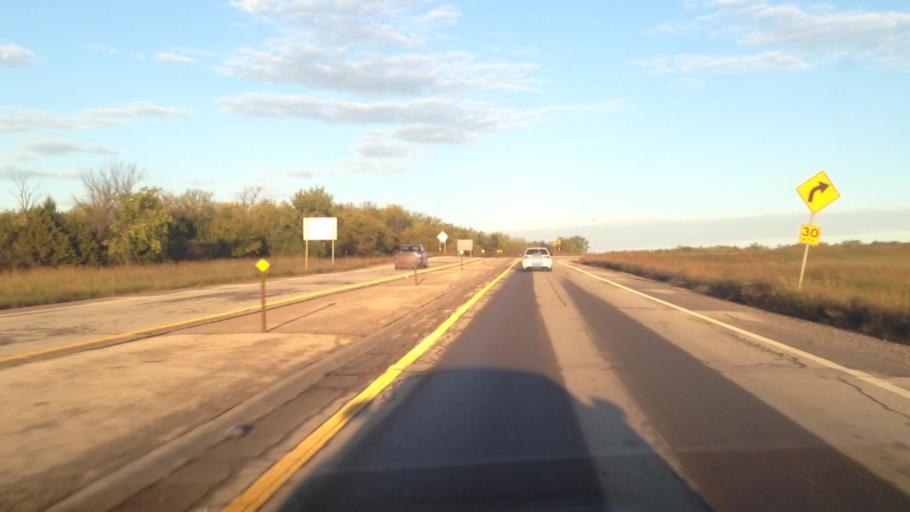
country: US
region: Kansas
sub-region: Johnson County
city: De Soto
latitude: 38.9590
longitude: -94.9850
